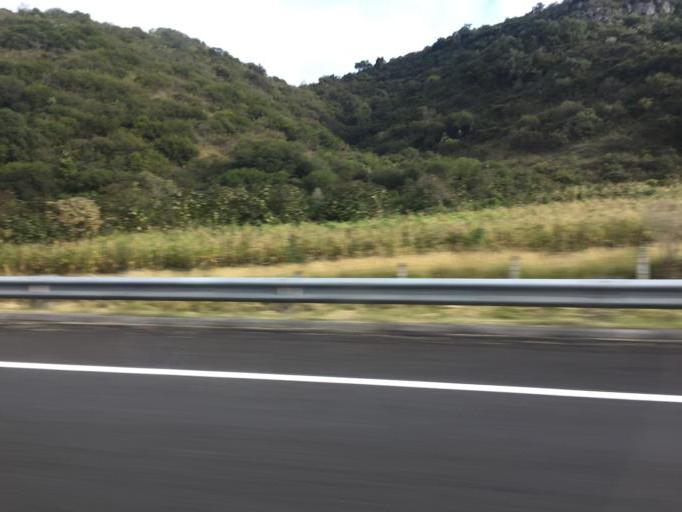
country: MX
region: Michoacan
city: Copandaro de Galeana
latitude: 19.8858
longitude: -101.1880
